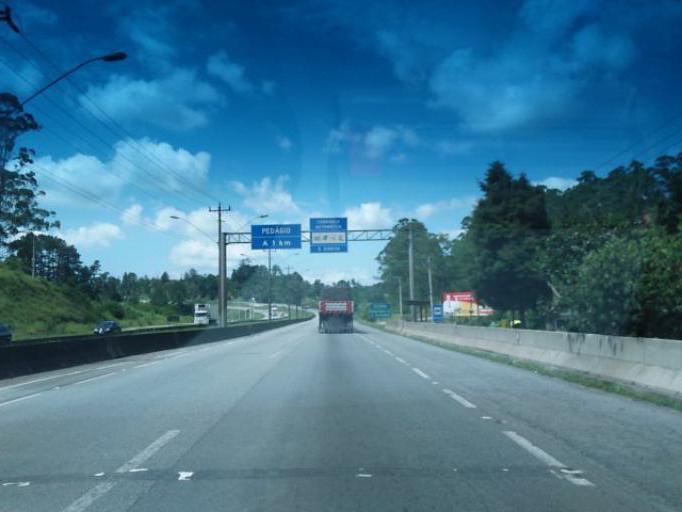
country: BR
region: Sao Paulo
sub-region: Sao Lourenco Da Serra
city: Sao Lourenco da Serra
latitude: -23.7747
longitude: -46.9142
